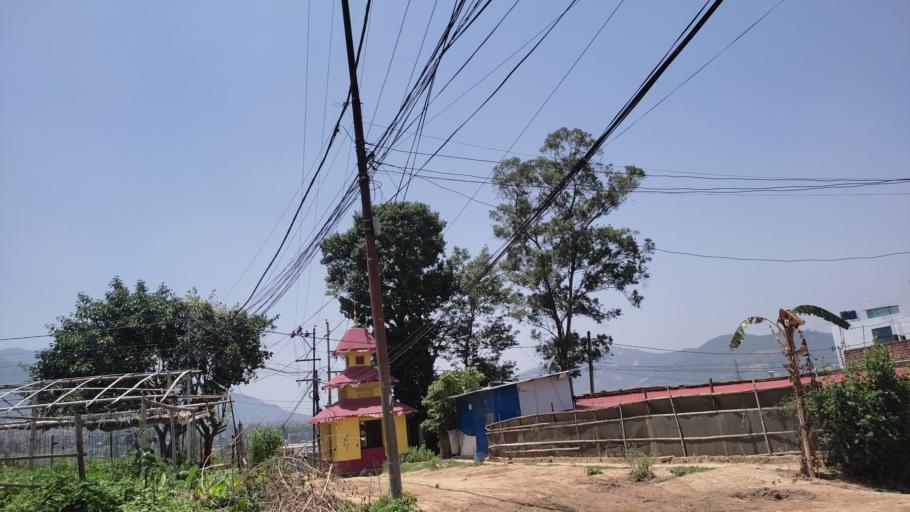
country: NP
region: Central Region
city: Kirtipur
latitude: 27.6702
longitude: 85.2619
